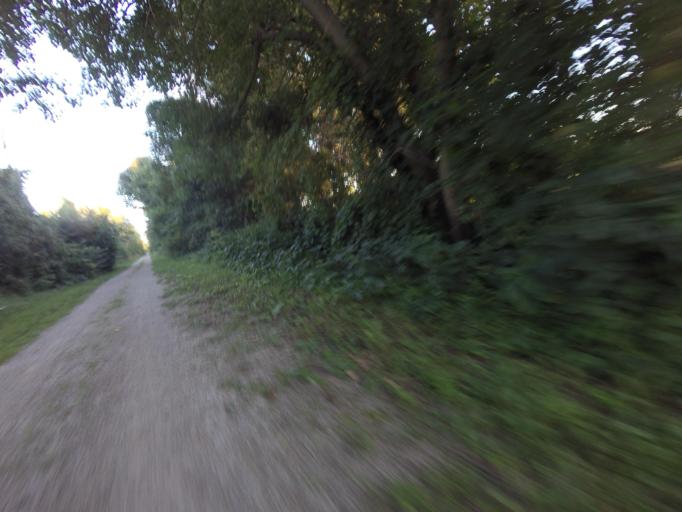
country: CA
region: Ontario
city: Goderich
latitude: 43.7551
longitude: -81.6750
